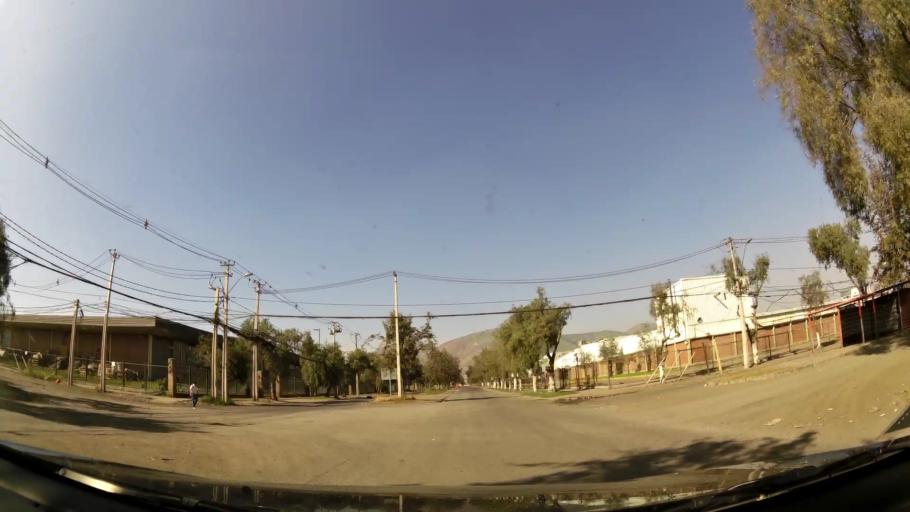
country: CL
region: Santiago Metropolitan
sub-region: Provincia de Chacabuco
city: Chicureo Abajo
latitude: -33.3285
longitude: -70.7260
